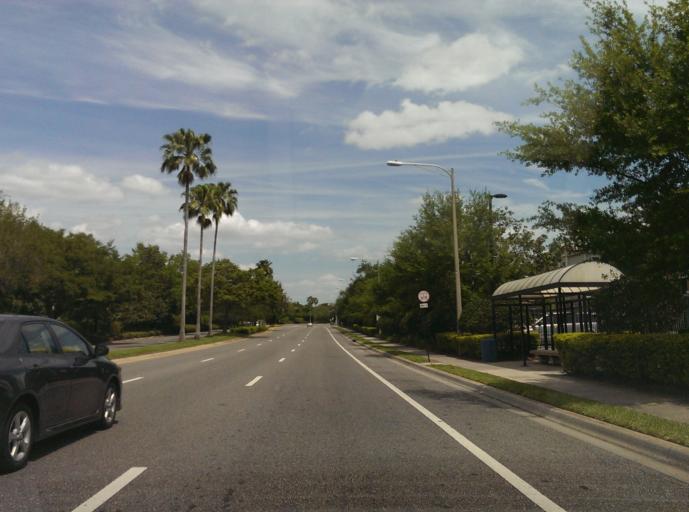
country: US
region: Florida
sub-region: Orange County
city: Tangelo Park
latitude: 28.4816
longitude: -81.4712
